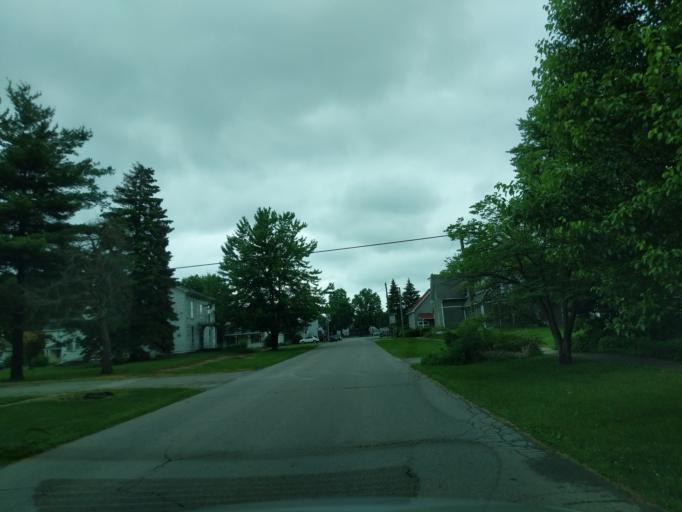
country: US
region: Indiana
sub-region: Hamilton County
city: Cicero
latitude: 40.1301
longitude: -86.0161
